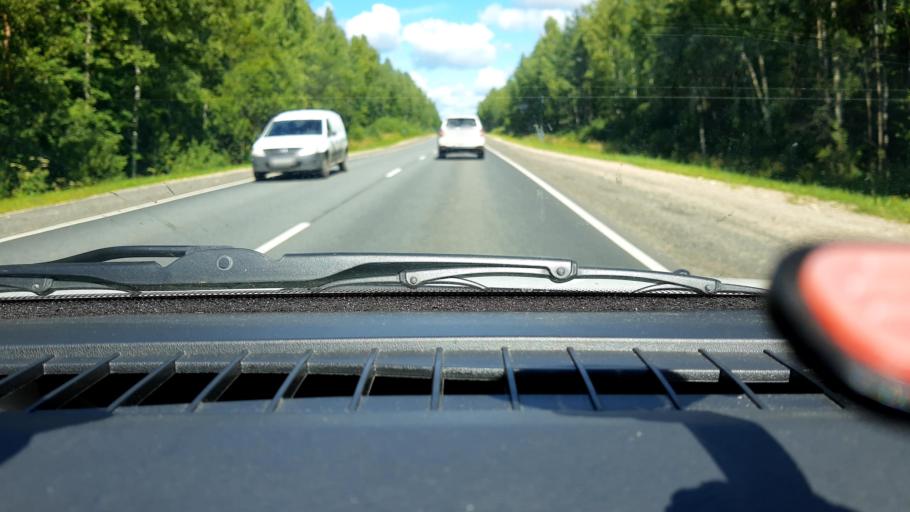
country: RU
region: Nizjnij Novgorod
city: Arzamas
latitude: 55.4461
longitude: 43.8874
